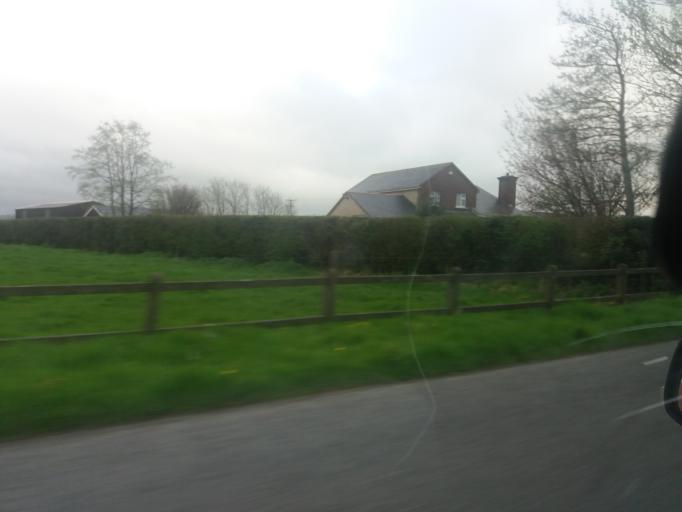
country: IE
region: Munster
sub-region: County Limerick
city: Newcastle West
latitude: 52.4778
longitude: -9.0144
